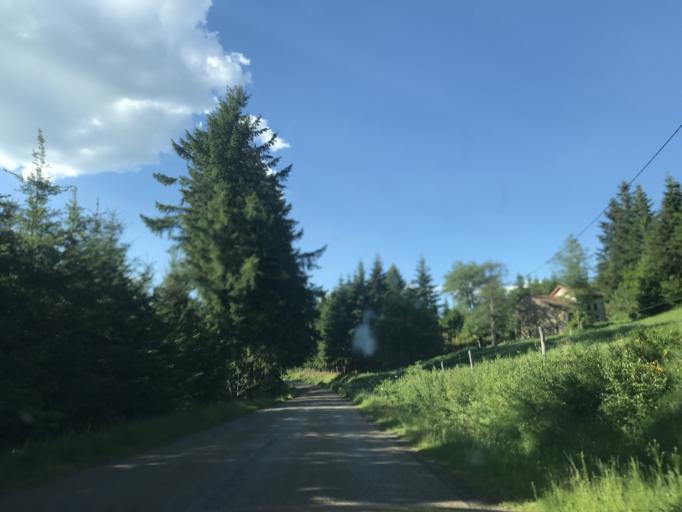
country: FR
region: Auvergne
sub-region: Departement du Puy-de-Dome
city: Job
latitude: 45.6073
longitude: 3.6561
